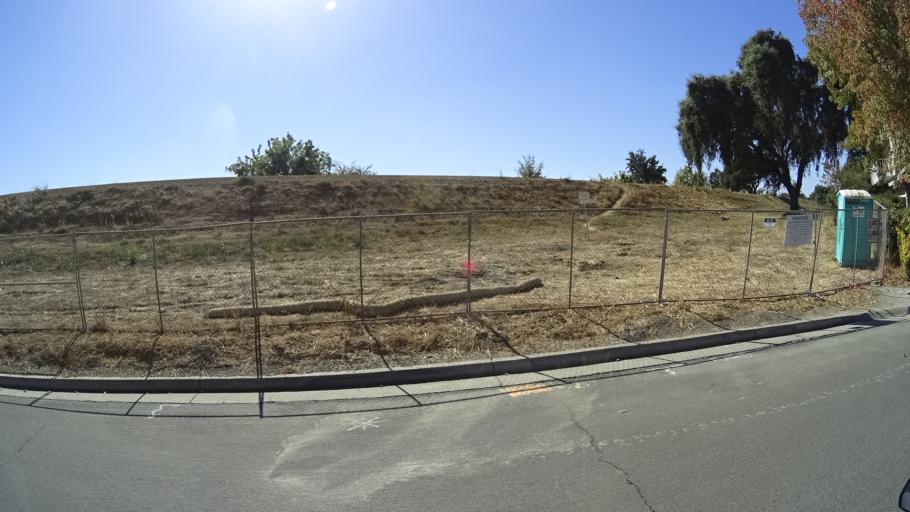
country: US
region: California
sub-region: Sacramento County
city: Parkway
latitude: 38.4750
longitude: -121.5112
